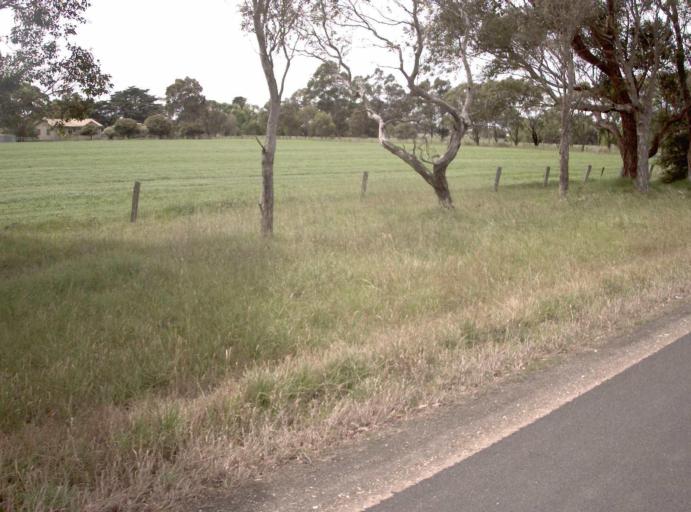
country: AU
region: Victoria
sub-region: Wellington
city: Sale
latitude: -38.0571
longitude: 147.0263
